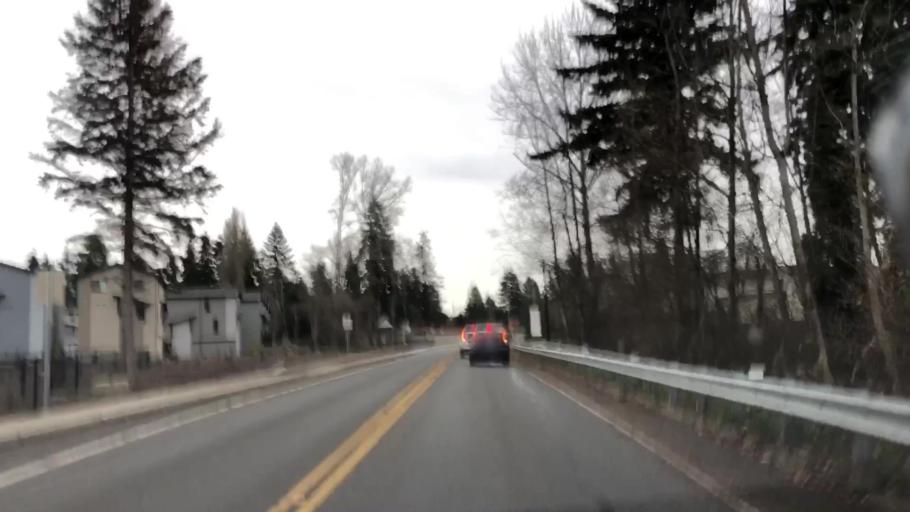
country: US
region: Washington
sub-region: Snohomish County
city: Martha Lake
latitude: 47.8354
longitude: -122.2597
